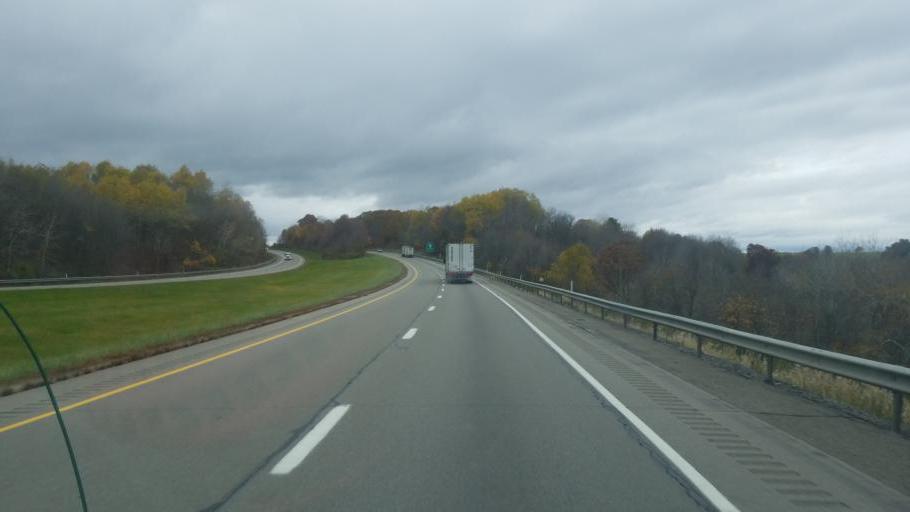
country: US
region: Pennsylvania
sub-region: Jefferson County
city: Brookville
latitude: 41.1878
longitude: -79.1742
